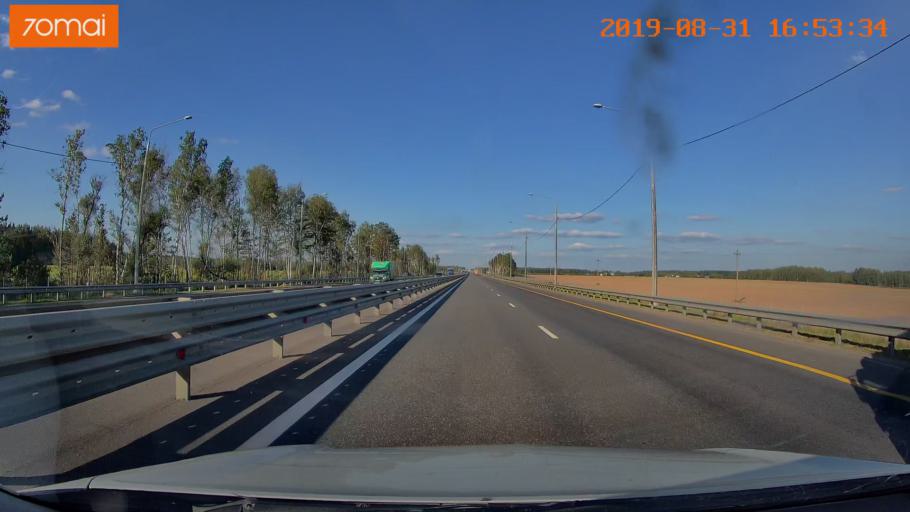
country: RU
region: Kaluga
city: Detchino
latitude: 54.7606
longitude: 36.2195
